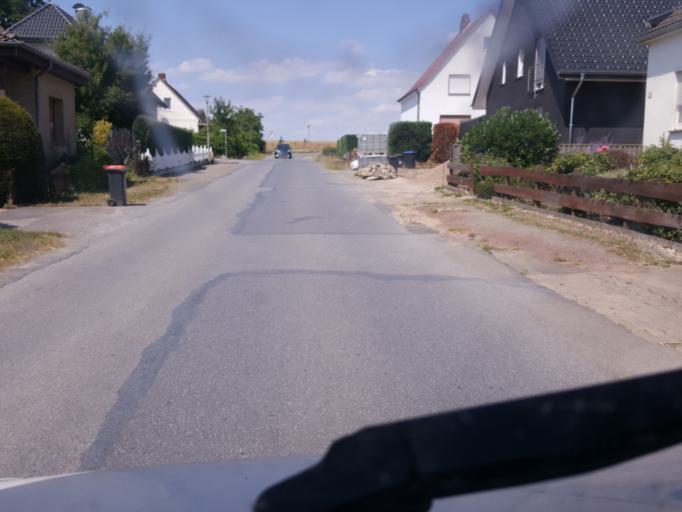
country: DE
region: North Rhine-Westphalia
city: Bad Oeynhausen
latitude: 52.2207
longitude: 8.7625
